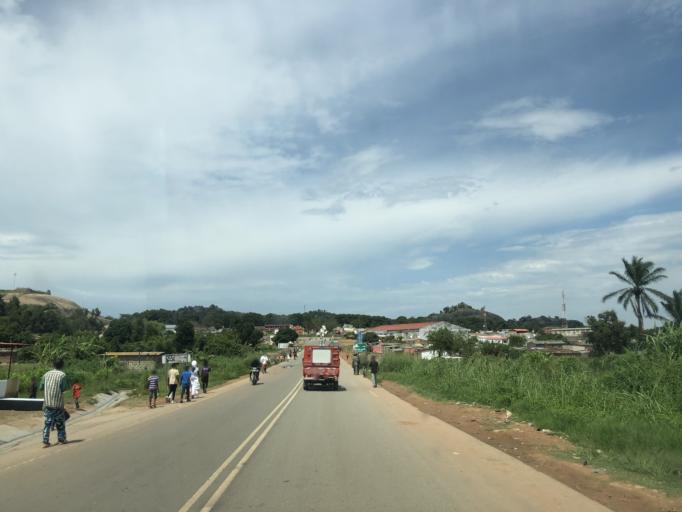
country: AO
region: Cuanza Sul
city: Quibala
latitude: -10.7356
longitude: 14.9856
